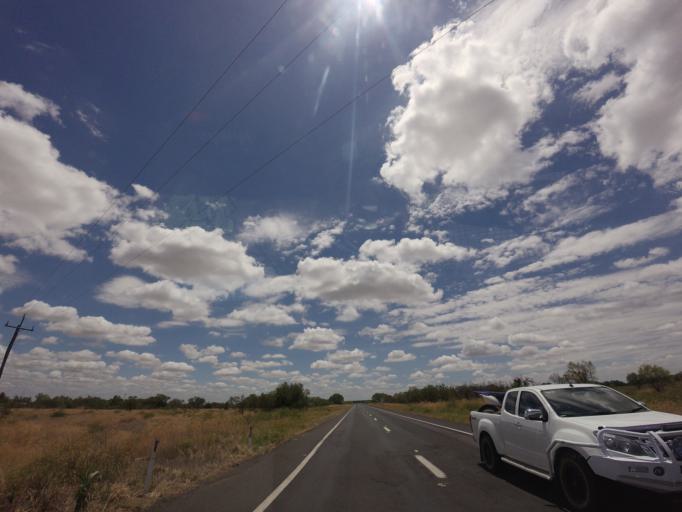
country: AU
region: New South Wales
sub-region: Moree Plains
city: Boggabilla
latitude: -28.9332
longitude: 150.1110
